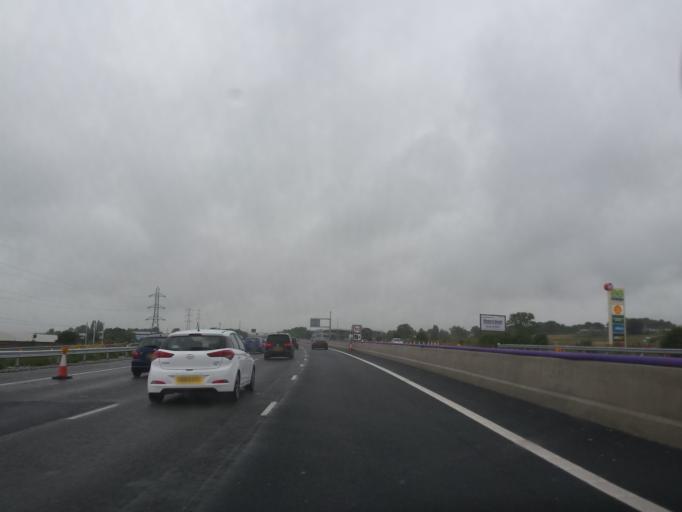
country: GB
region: England
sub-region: Derbyshire
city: Staveley
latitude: 53.2438
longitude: -1.3321
